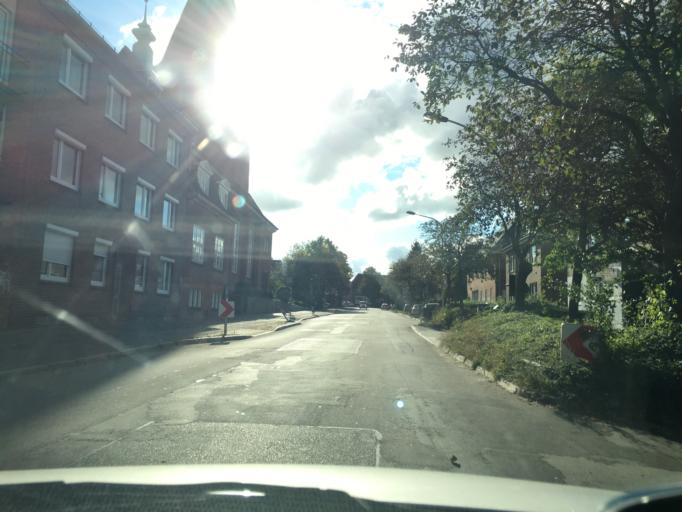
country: DE
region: Schleswig-Holstein
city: Kiel
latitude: 54.3039
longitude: 10.1087
